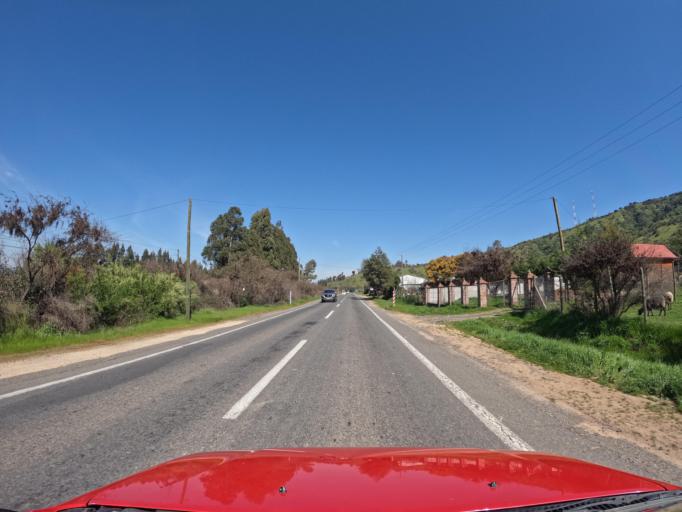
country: CL
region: Maule
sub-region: Provincia de Talca
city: Talca
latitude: -35.0831
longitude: -71.6406
